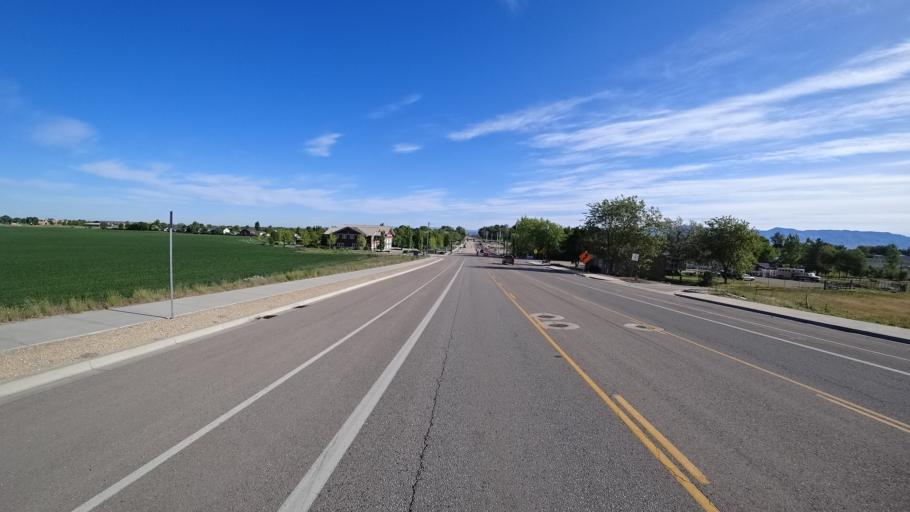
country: US
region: Idaho
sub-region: Ada County
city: Garden City
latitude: 43.5655
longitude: -116.2742
